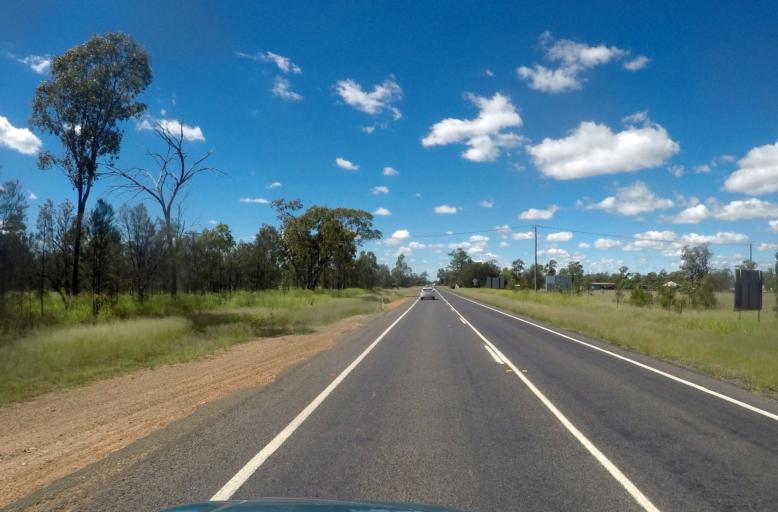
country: AU
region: Queensland
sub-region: Western Downs
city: Westcourt
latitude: -26.6733
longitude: 150.3382
